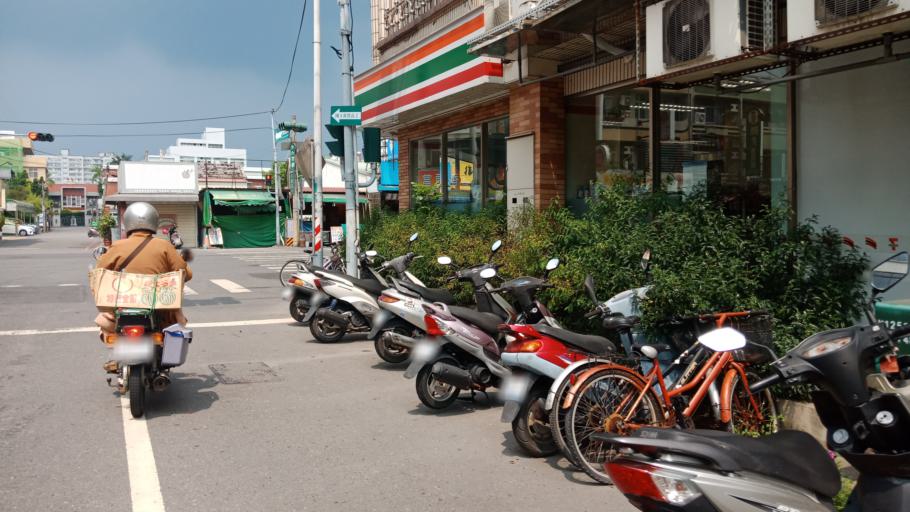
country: TW
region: Taiwan
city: Xinying
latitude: 23.3109
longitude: 120.3226
